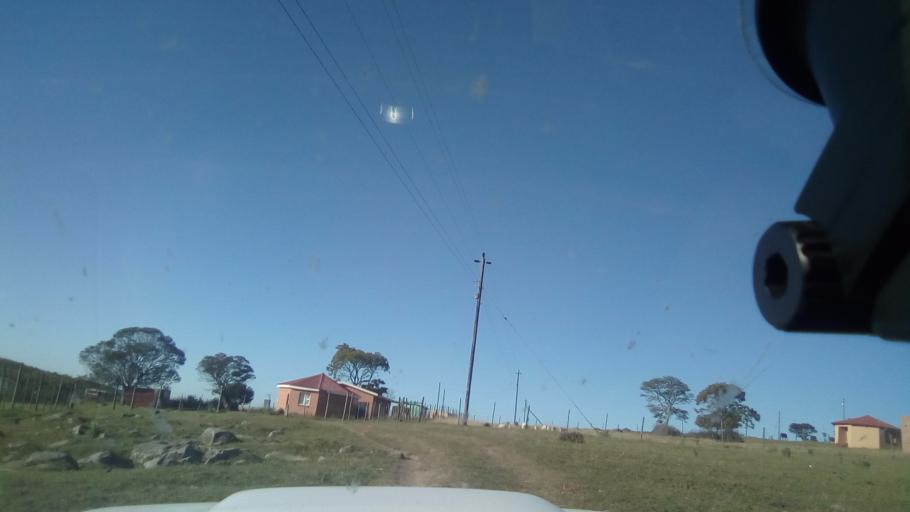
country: ZA
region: Eastern Cape
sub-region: Buffalo City Metropolitan Municipality
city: Bhisho
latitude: -32.9466
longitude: 27.2914
